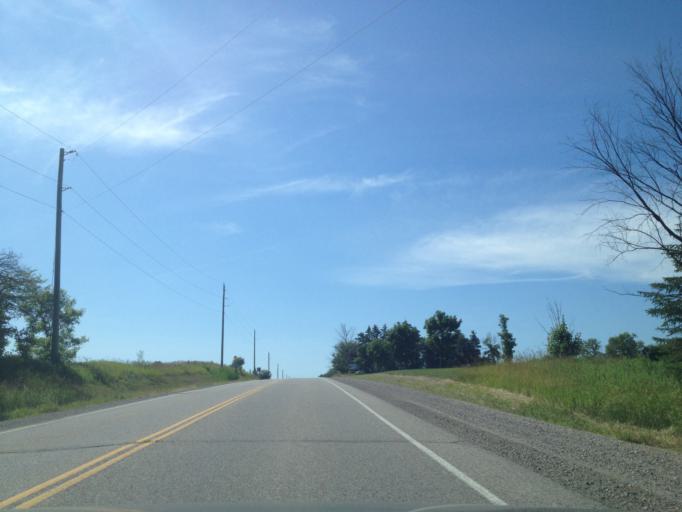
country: CA
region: Ontario
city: Stratford
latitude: 43.4692
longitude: -80.7984
